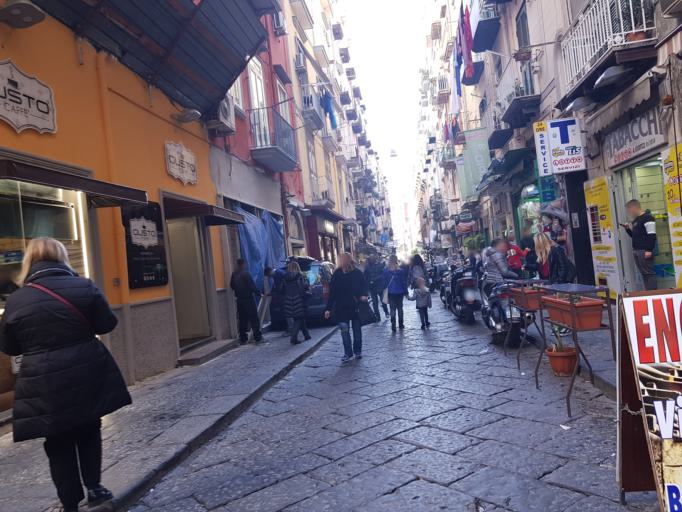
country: IT
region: Campania
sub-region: Provincia di Napoli
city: Napoli
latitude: 40.8455
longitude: 14.2481
